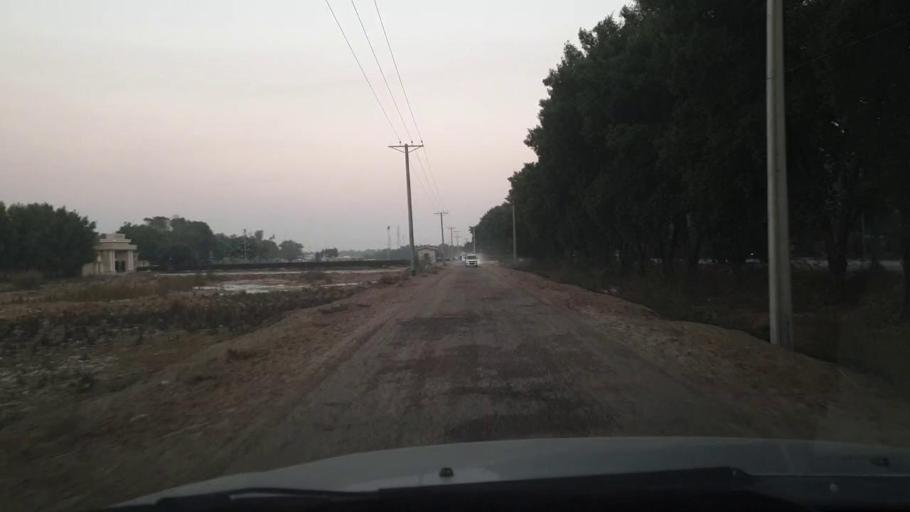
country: PK
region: Sindh
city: Mirpur Mathelo
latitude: 28.0277
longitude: 69.5776
